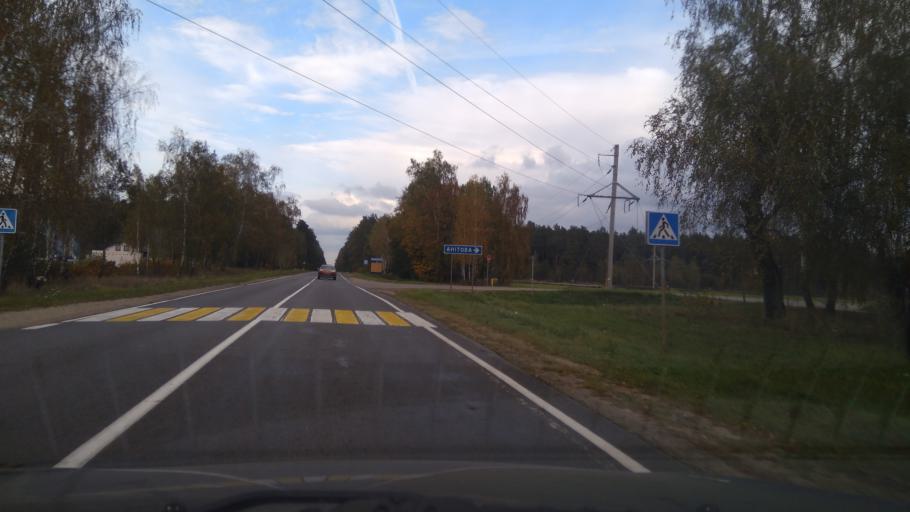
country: BY
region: Minsk
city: Rudzyensk
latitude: 53.6237
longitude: 27.8665
